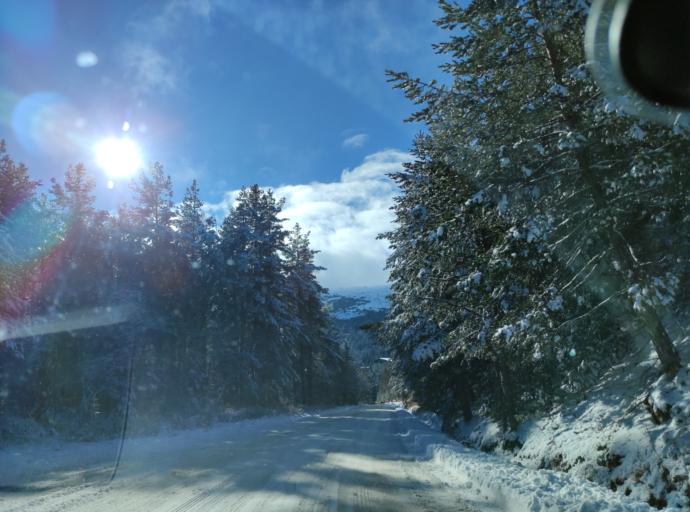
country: BG
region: Sofia-Capital
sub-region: Stolichna Obshtina
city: Sofia
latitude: 42.5911
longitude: 23.3001
